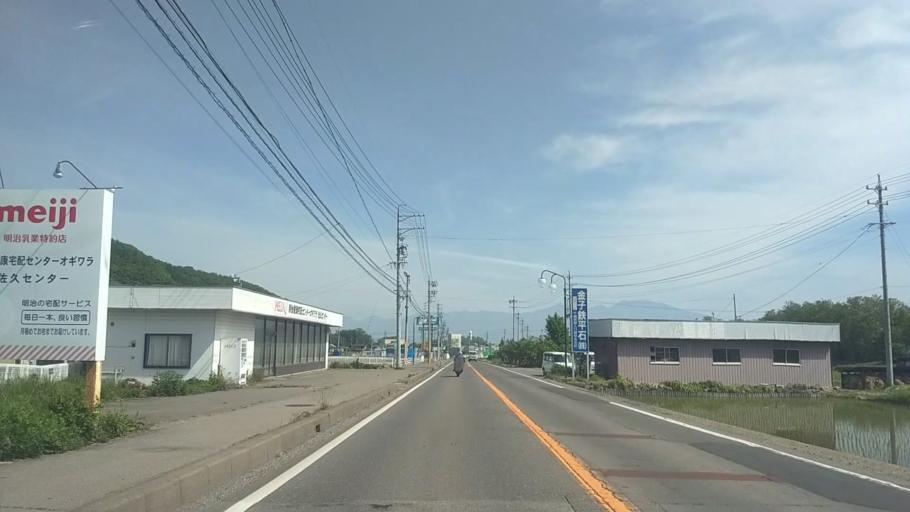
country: JP
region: Nagano
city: Saku
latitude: 36.1723
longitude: 138.4855
